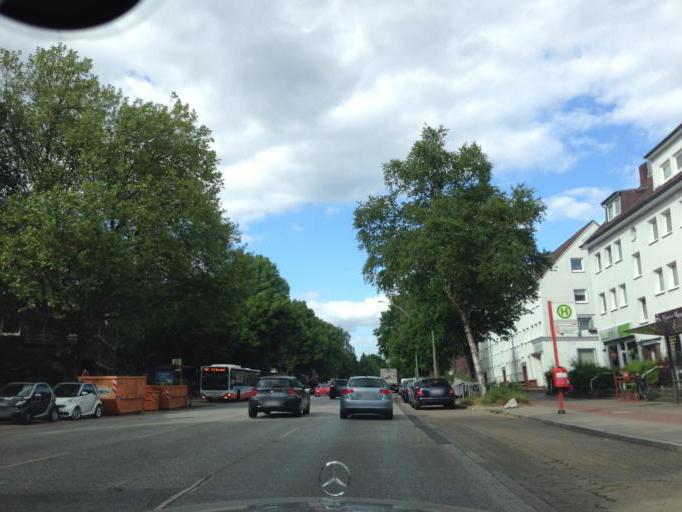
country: DE
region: Hamburg
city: Steilshoop
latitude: 53.5945
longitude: 10.0603
